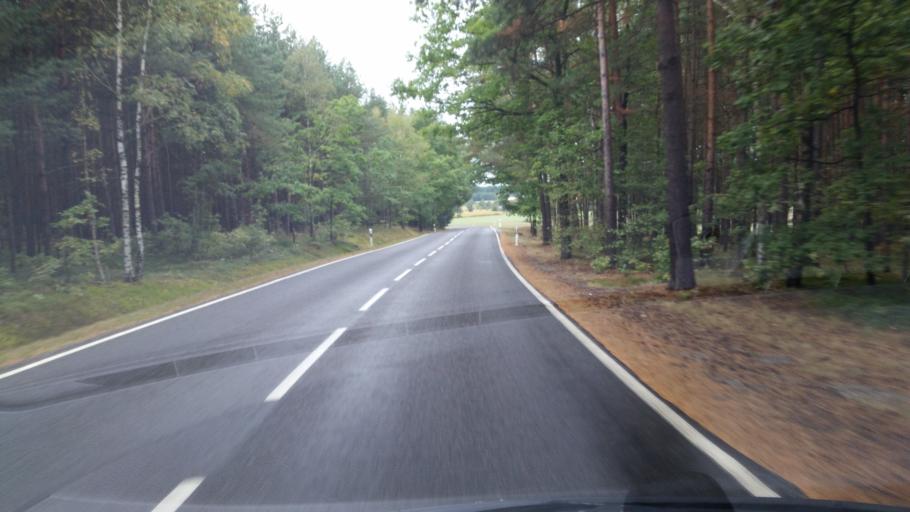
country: DE
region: Saxony
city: Neukirch
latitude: 51.3089
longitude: 14.0371
